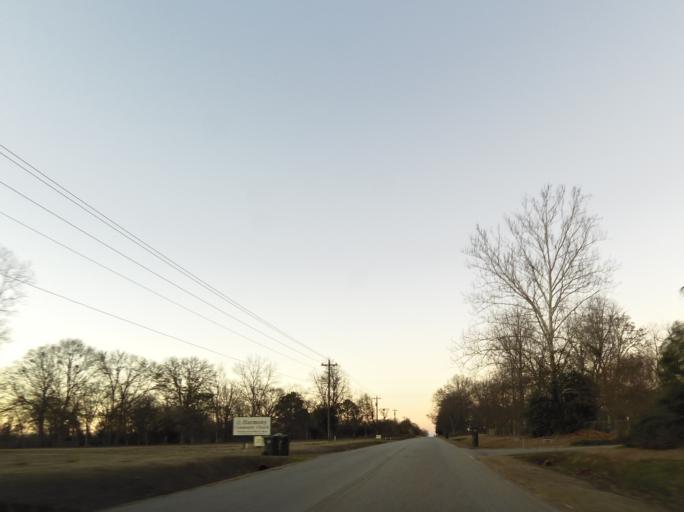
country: US
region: Georgia
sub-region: Peach County
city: Byron
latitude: 32.5902
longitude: -83.7482
